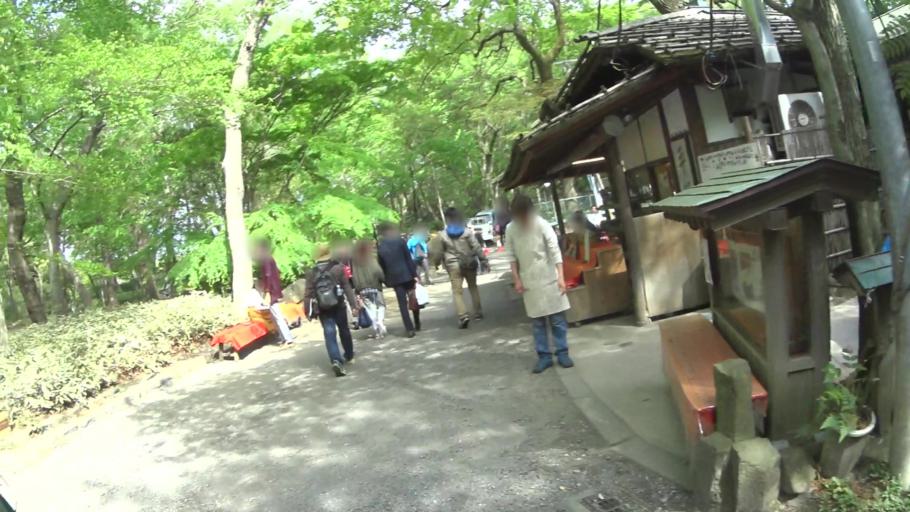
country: JP
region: Tokyo
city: Chofugaoka
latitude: 35.6684
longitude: 139.5496
